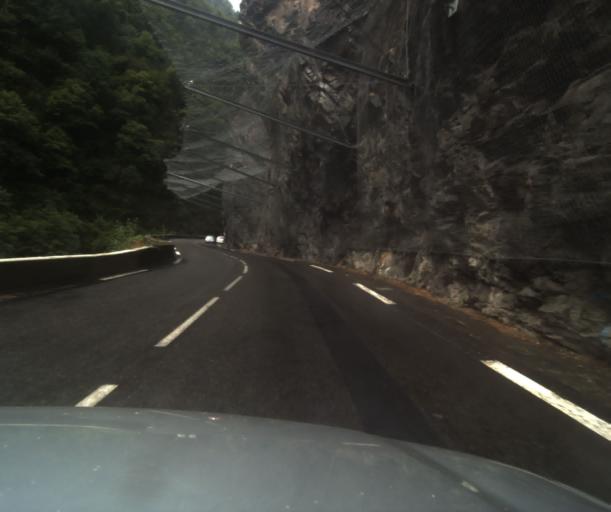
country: FR
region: Midi-Pyrenees
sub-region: Departement des Hautes-Pyrenees
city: Pierrefitte-Nestalas
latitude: 42.9344
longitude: -0.0477
